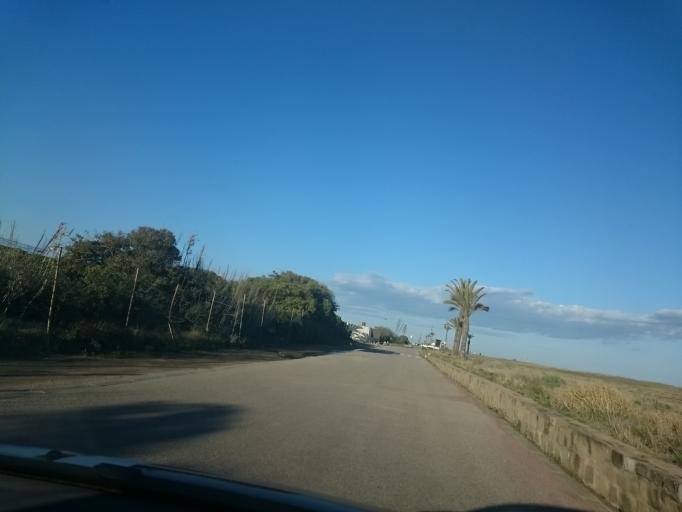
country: ES
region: Catalonia
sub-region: Provincia de Barcelona
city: El Prat de Llobregat
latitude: 41.2831
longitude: 2.0916
